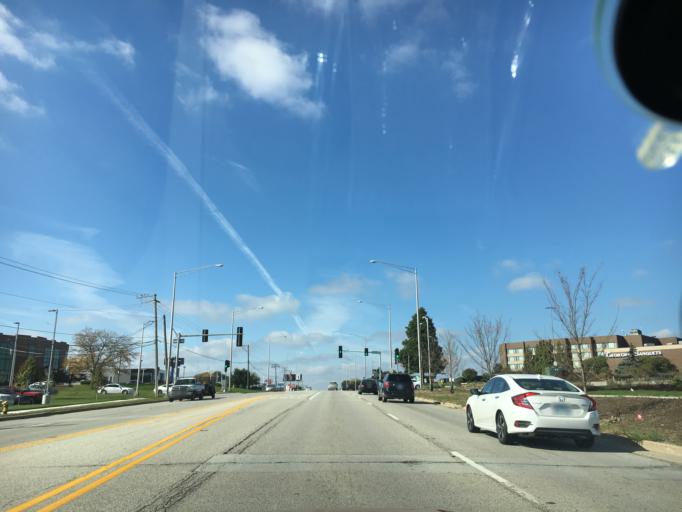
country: US
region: Illinois
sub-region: Cook County
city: Orland Hills
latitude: 41.6018
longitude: -87.8278
